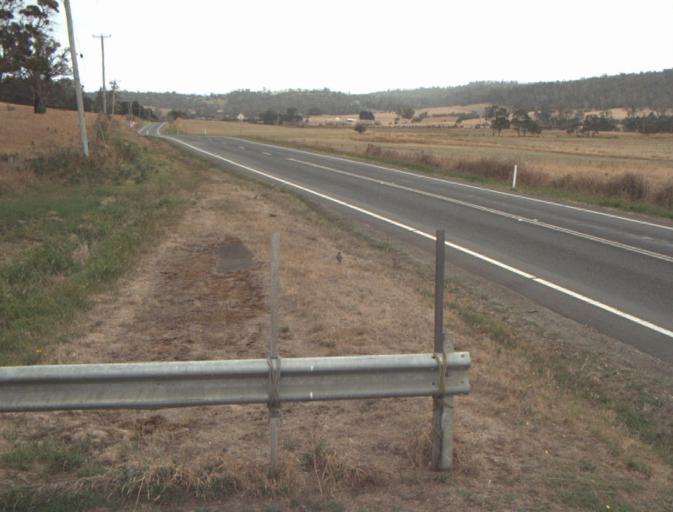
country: AU
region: Tasmania
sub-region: Launceston
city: Mayfield
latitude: -41.3250
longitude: 147.0642
